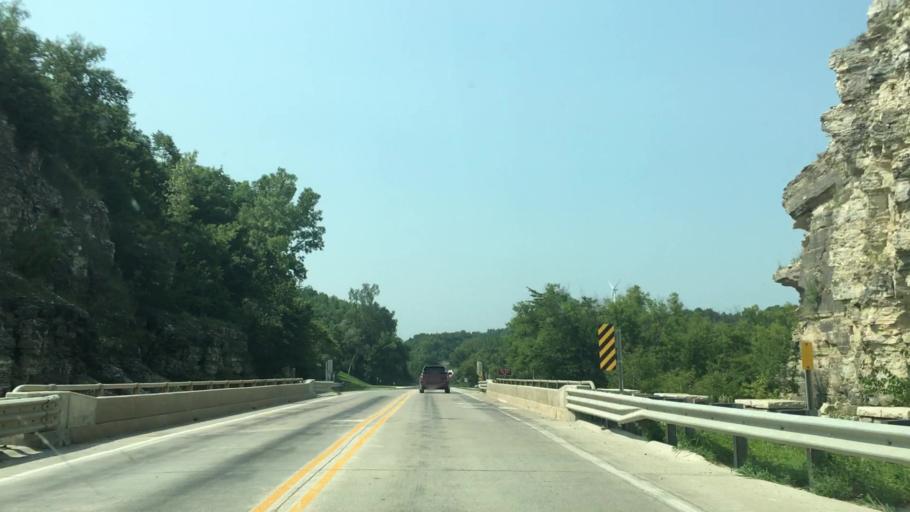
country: US
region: Iowa
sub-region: Winneshiek County
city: Decorah
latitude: 43.2955
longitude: -91.8086
